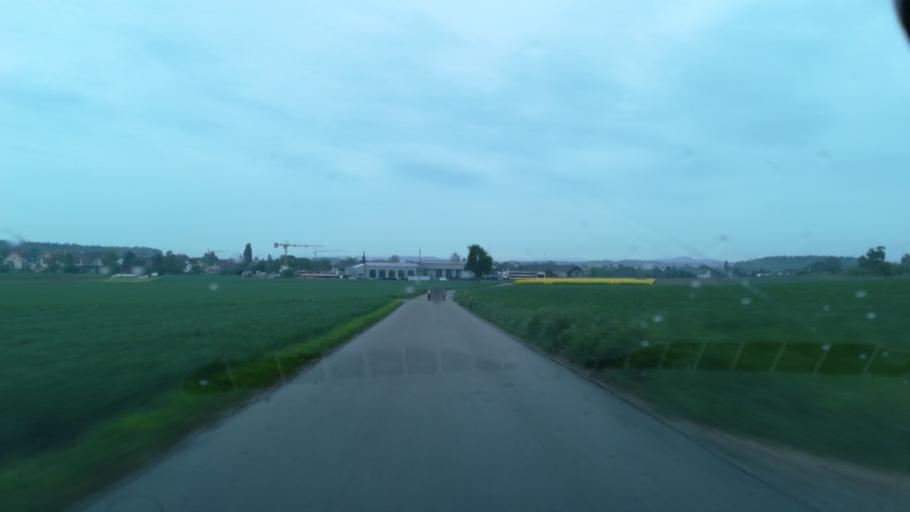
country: CH
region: Zurich
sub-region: Bezirk Buelach
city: End-Hoeri
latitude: 47.5144
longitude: 8.5014
